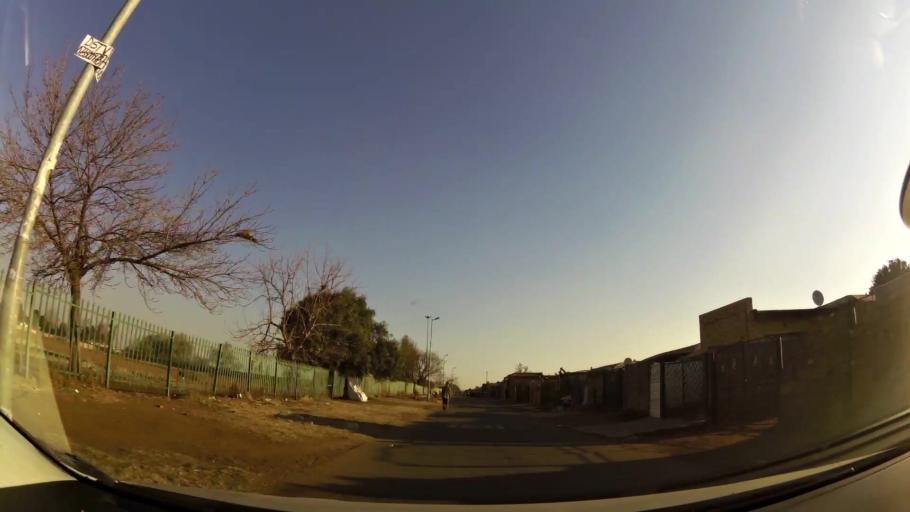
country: ZA
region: Gauteng
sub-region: City of Johannesburg Metropolitan Municipality
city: Soweto
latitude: -26.2540
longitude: 27.8828
